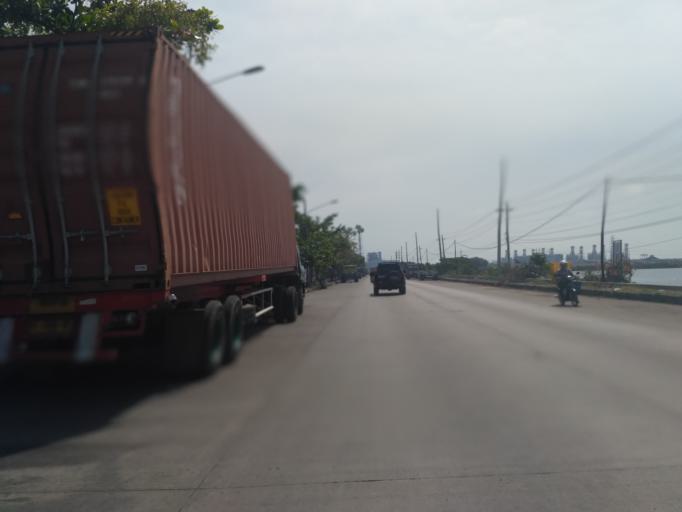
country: ID
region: Central Java
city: Semarang
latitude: -6.9629
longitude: 110.4308
